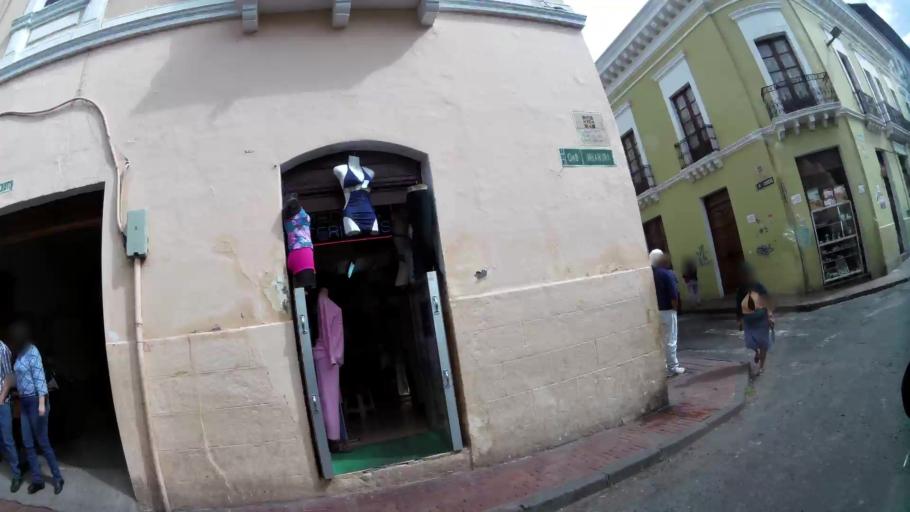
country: EC
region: Pichincha
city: Quito
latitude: -0.2184
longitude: -78.5159
